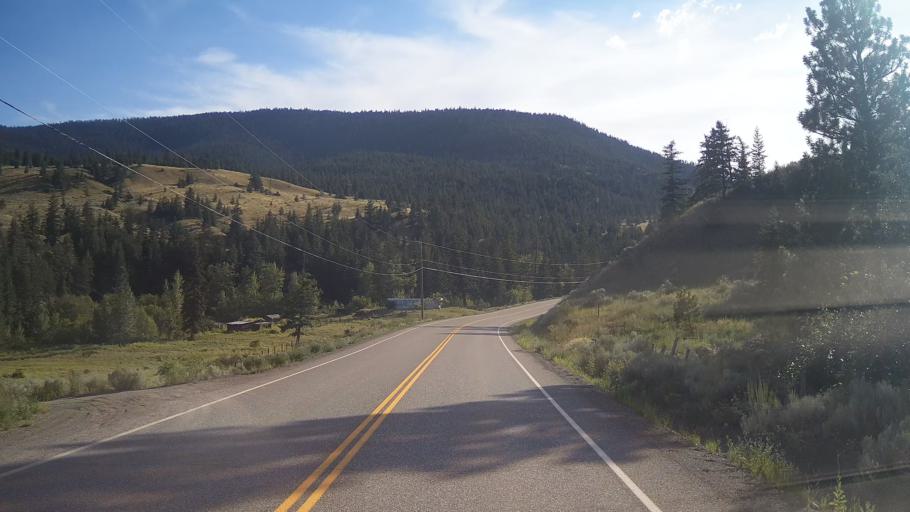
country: CA
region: British Columbia
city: Cache Creek
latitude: 50.8851
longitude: -121.4707
